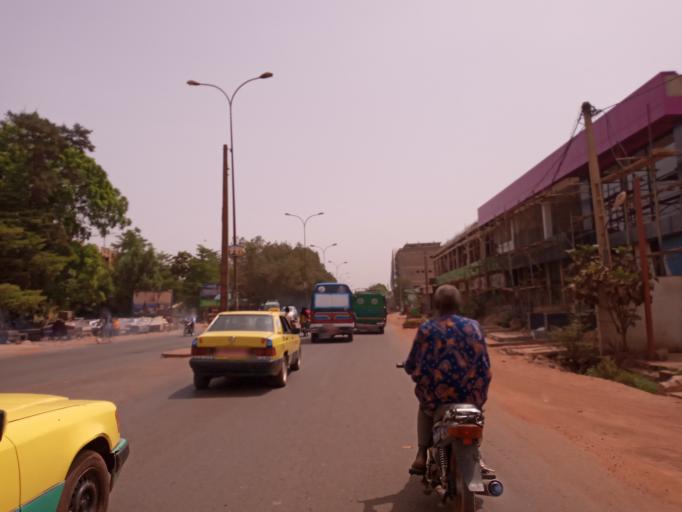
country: ML
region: Bamako
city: Bamako
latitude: 12.6550
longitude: -7.9755
